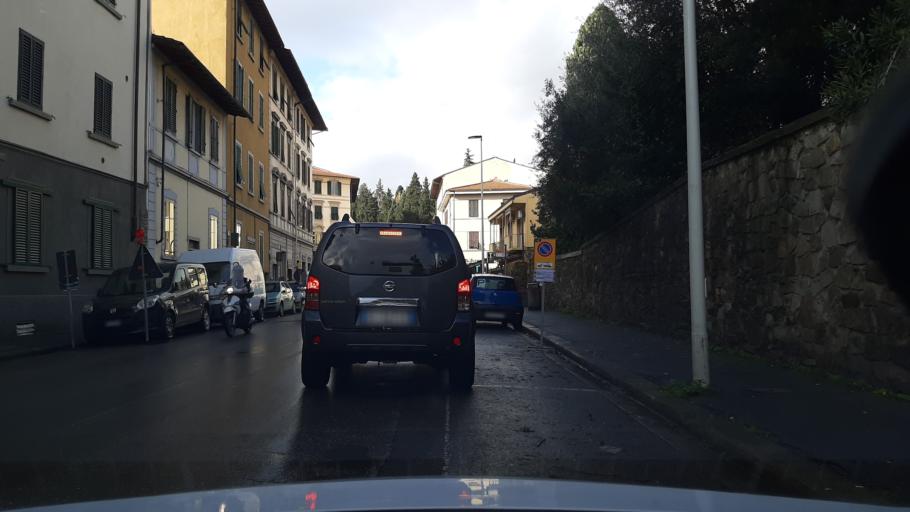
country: IT
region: Tuscany
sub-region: Province of Florence
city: Florence
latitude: 43.7922
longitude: 11.2520
